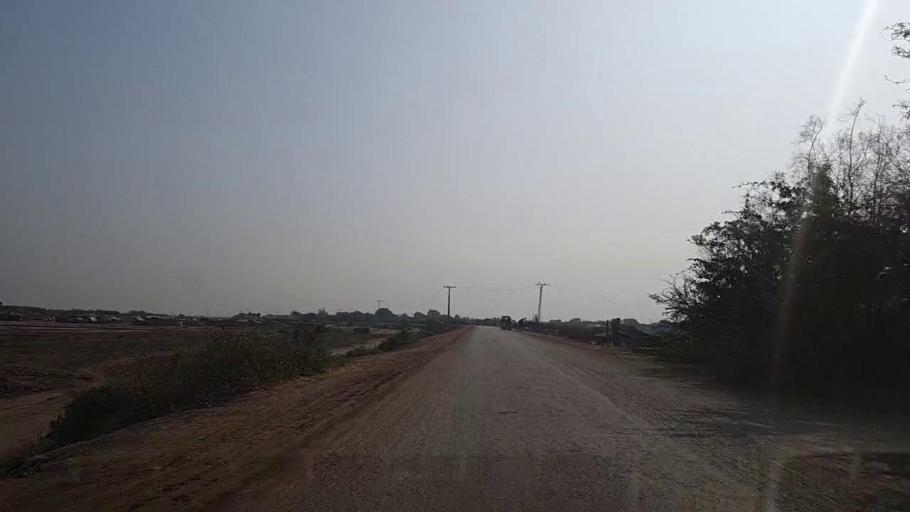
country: PK
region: Sindh
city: Keti Bandar
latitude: 24.2348
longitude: 67.6080
